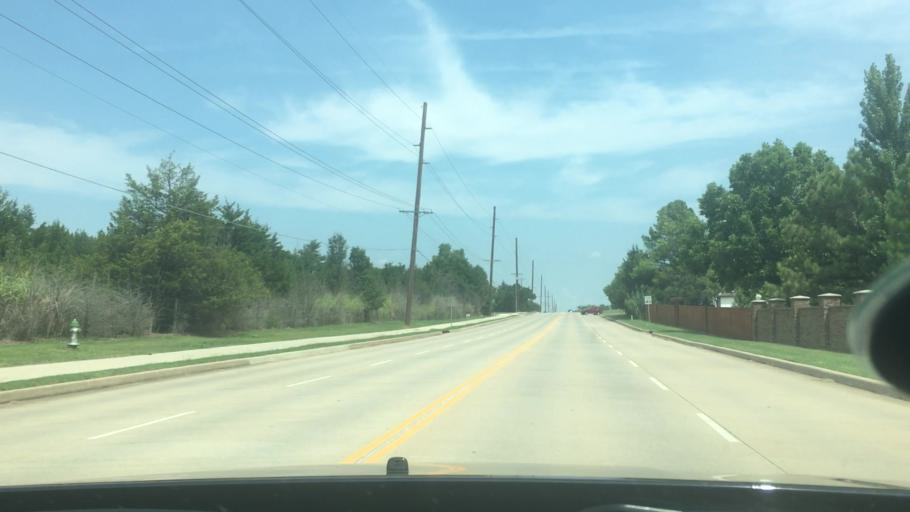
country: US
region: Oklahoma
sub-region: Pottawatomie County
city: Shawnee
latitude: 35.3563
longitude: -96.8942
